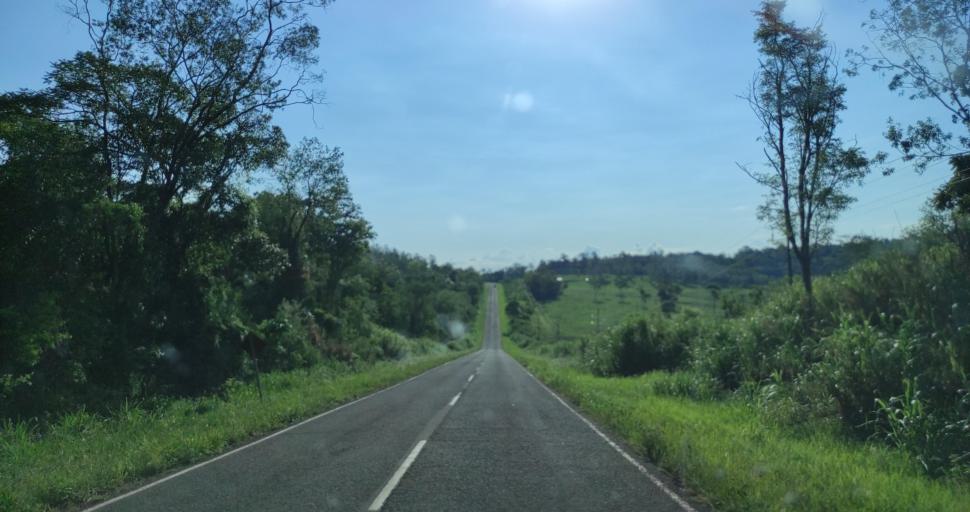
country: AR
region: Misiones
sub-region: Departamento de Eldorado
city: Eldorado
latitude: -26.3757
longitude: -54.3283
